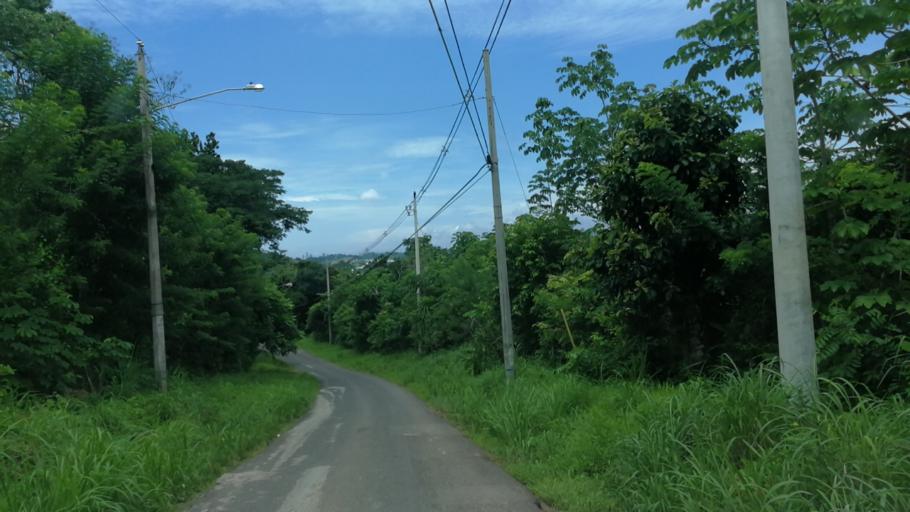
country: PA
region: Panama
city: San Miguelito
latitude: 9.1052
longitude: -79.4555
